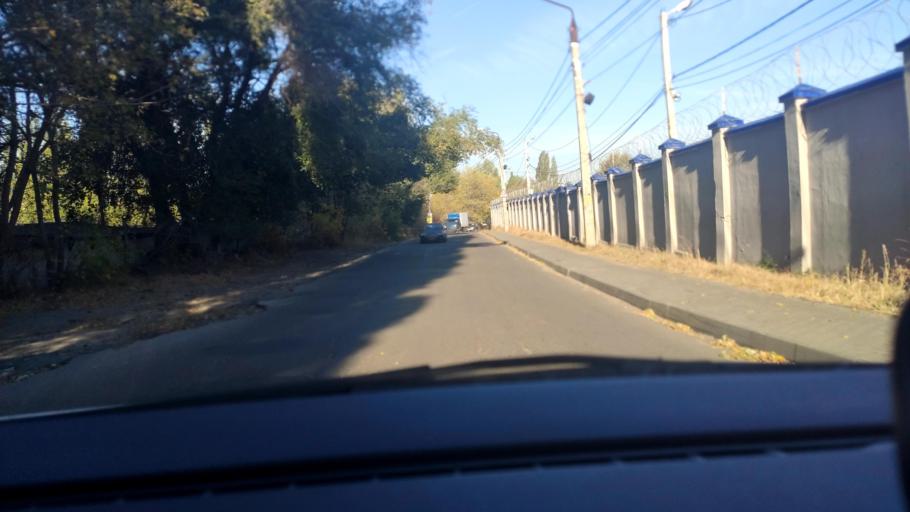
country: RU
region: Voronezj
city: Voronezh
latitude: 51.6586
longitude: 39.1365
